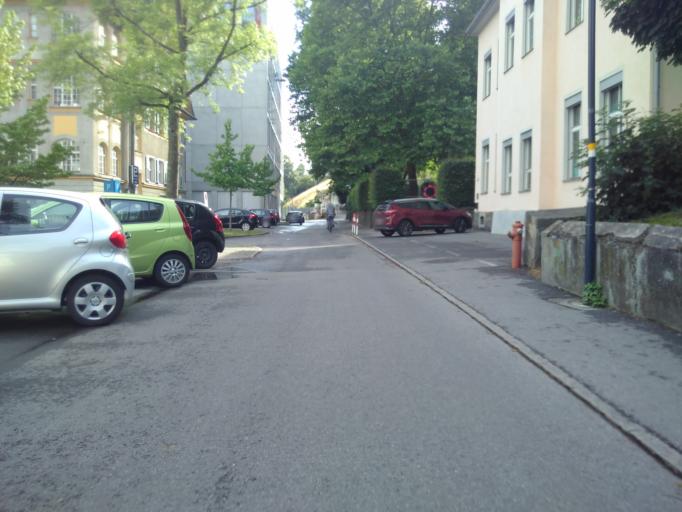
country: AT
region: Vorarlberg
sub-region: Politischer Bezirk Feldkirch
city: Feldkirch
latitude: 47.2404
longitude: 9.5978
